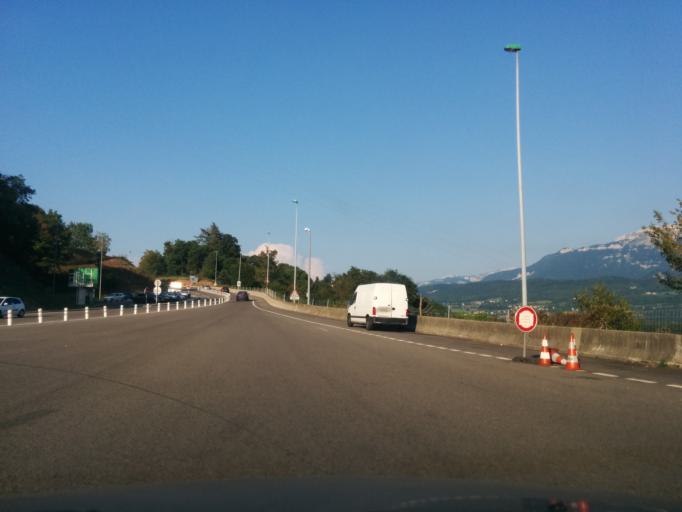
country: FR
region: Rhone-Alpes
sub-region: Departement de l'Isere
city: Saint-Cassien
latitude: 45.3475
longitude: 5.5670
